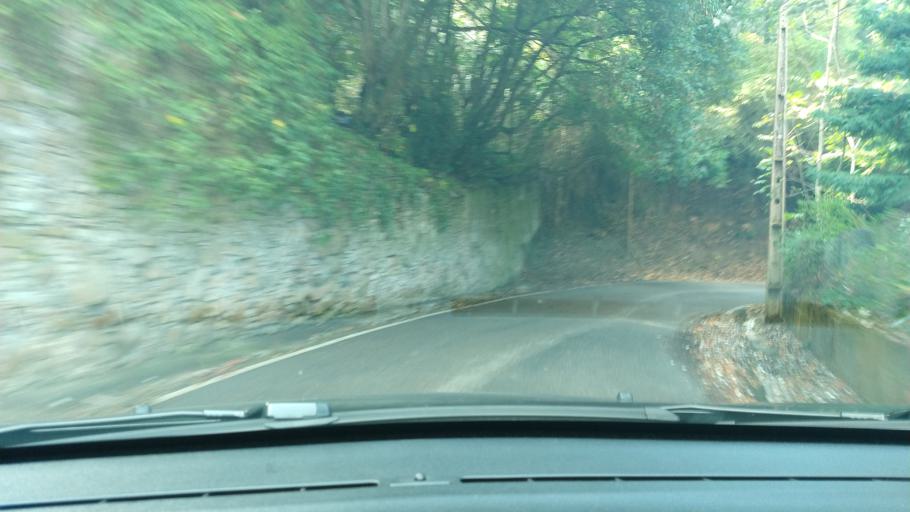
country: PT
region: Lisbon
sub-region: Sintra
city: Colares
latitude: 38.7951
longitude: -9.4358
